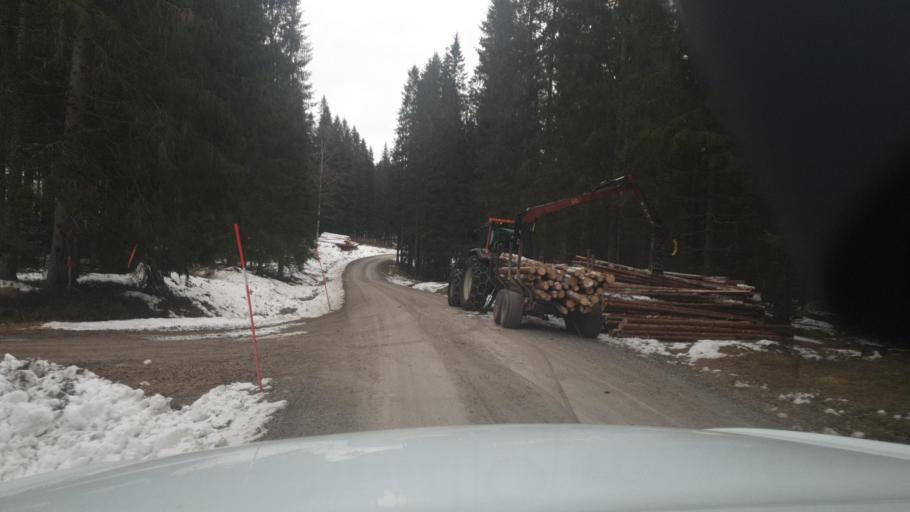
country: SE
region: Vaermland
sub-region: Sunne Kommun
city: Sunne
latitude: 59.8576
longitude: 12.8866
